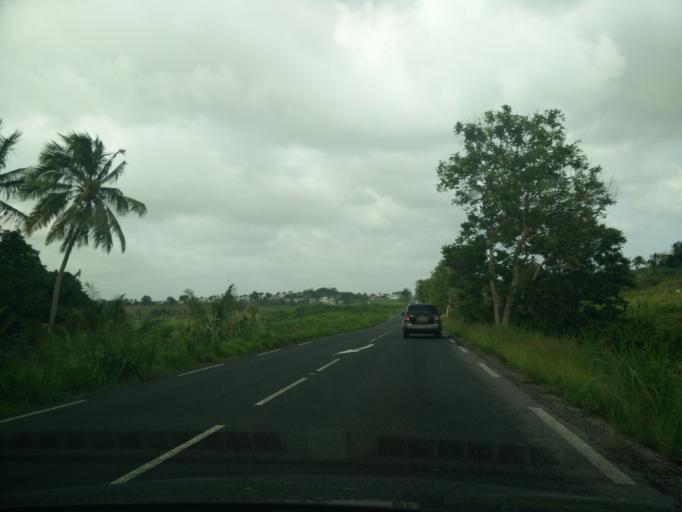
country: GP
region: Guadeloupe
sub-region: Guadeloupe
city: Petit-Bourg
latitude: 16.2168
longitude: -61.6115
